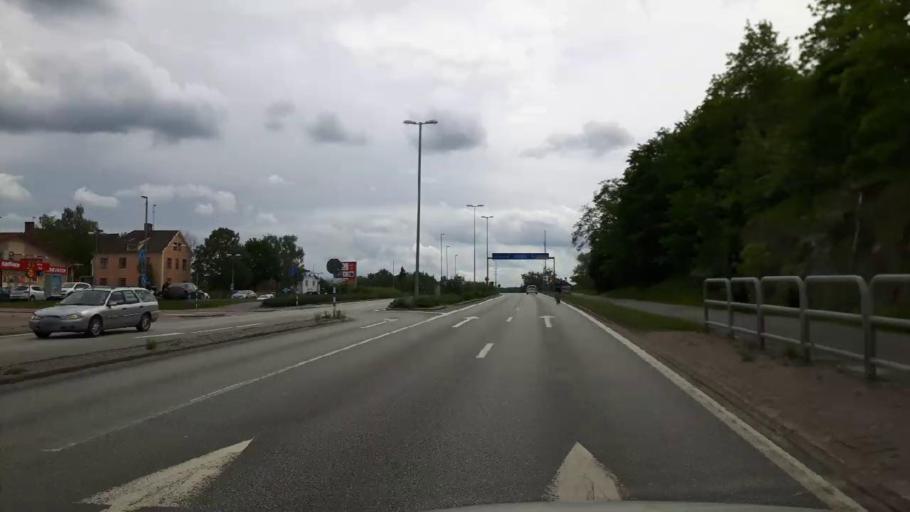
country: SE
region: Vaestmanland
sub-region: Fagersta Kommun
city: Fagersta
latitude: 59.9898
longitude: 15.8134
